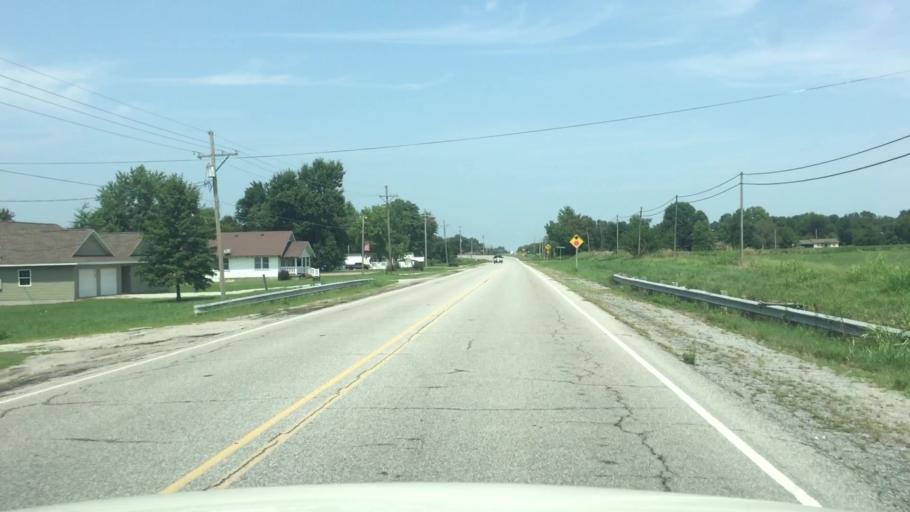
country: US
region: Kansas
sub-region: Cherokee County
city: Galena
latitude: 37.0812
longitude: -94.7044
